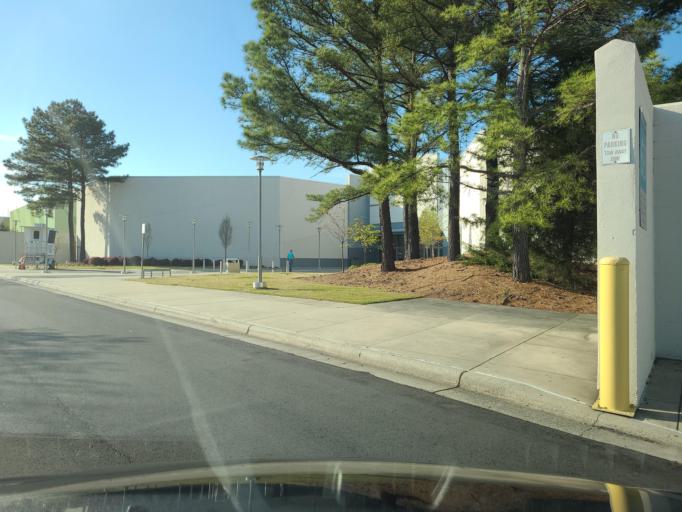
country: US
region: North Carolina
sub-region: Cabarrus County
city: Harrisburg
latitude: 35.3680
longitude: -80.7224
